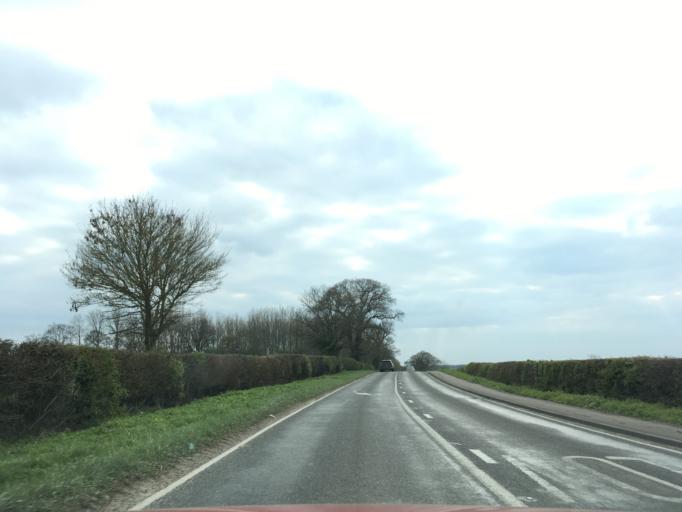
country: GB
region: England
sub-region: Oxfordshire
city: North Leigh
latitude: 51.8061
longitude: -1.4444
